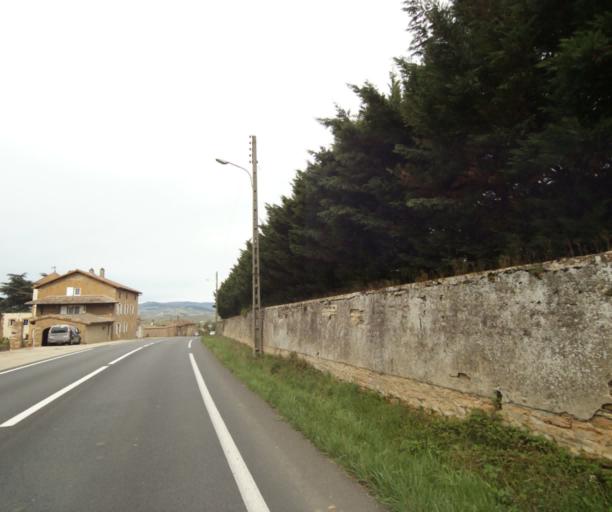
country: FR
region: Bourgogne
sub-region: Departement de Saone-et-Loire
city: Charnay-les-Macon
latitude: 46.3138
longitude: 4.7830
